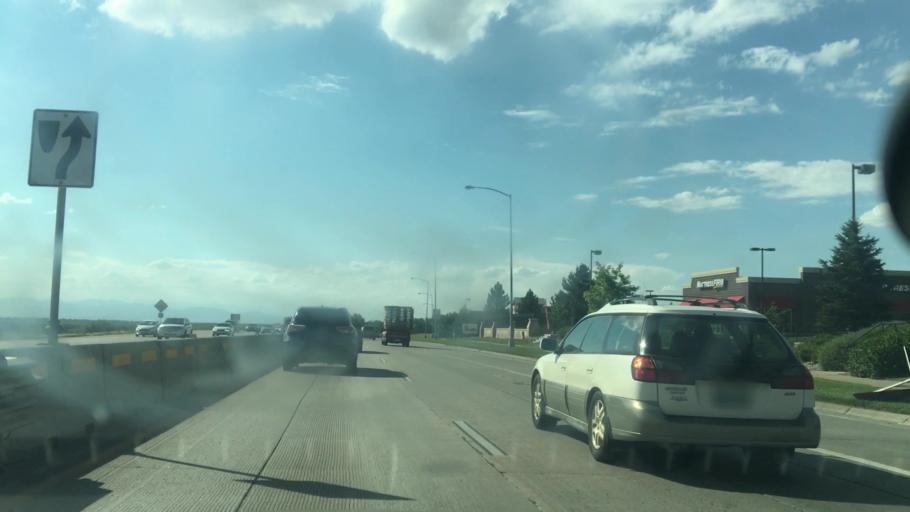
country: US
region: Colorado
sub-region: Arapahoe County
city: Dove Valley
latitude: 39.6145
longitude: -104.8154
